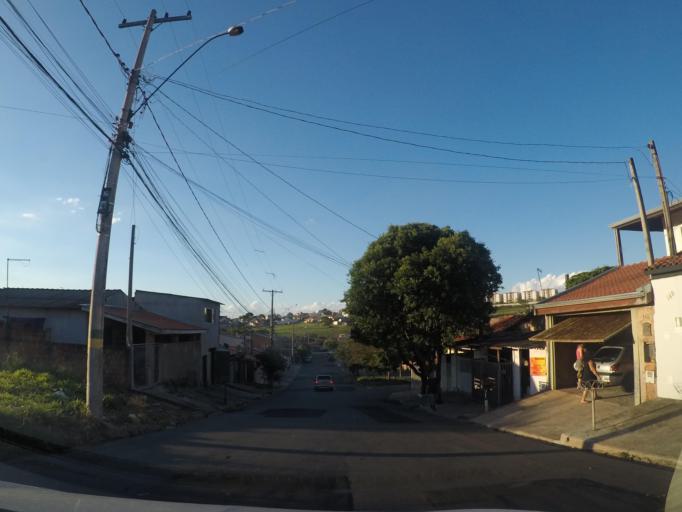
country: BR
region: Sao Paulo
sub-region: Sumare
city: Sumare
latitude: -22.8256
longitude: -47.2484
